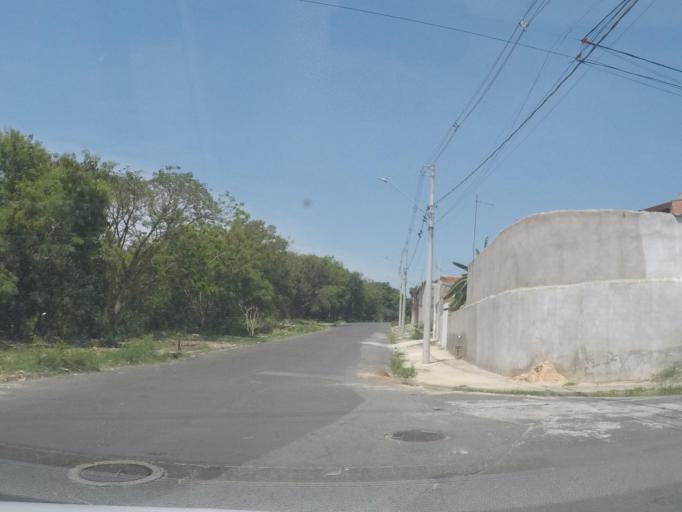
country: BR
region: Sao Paulo
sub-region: Hortolandia
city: Hortolandia
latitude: -22.8572
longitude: -47.1999
